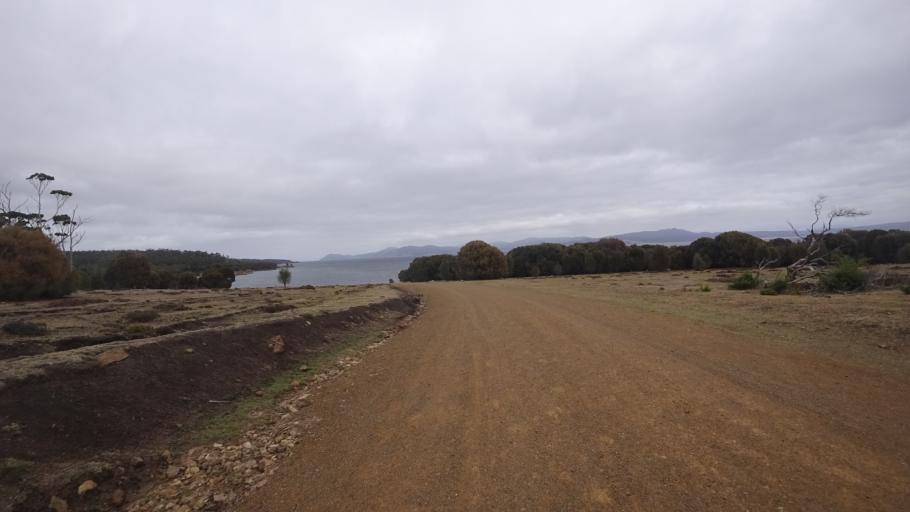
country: AU
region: Tasmania
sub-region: Sorell
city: Sorell
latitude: -42.5849
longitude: 148.0549
